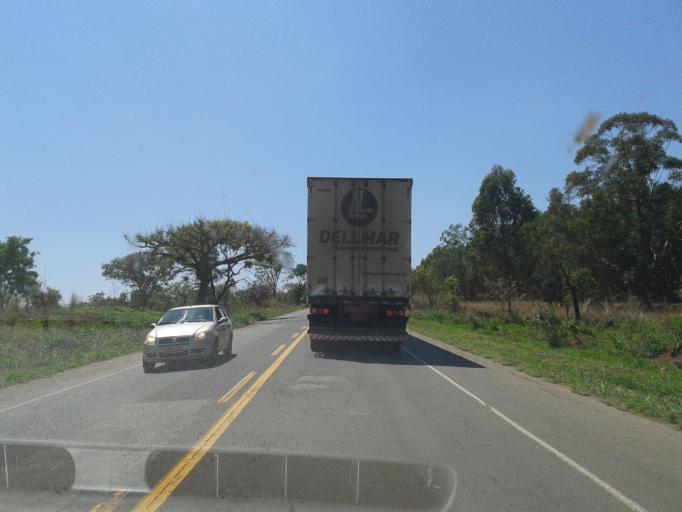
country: BR
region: Minas Gerais
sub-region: Araxa
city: Araxa
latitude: -19.4356
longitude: -47.2065
